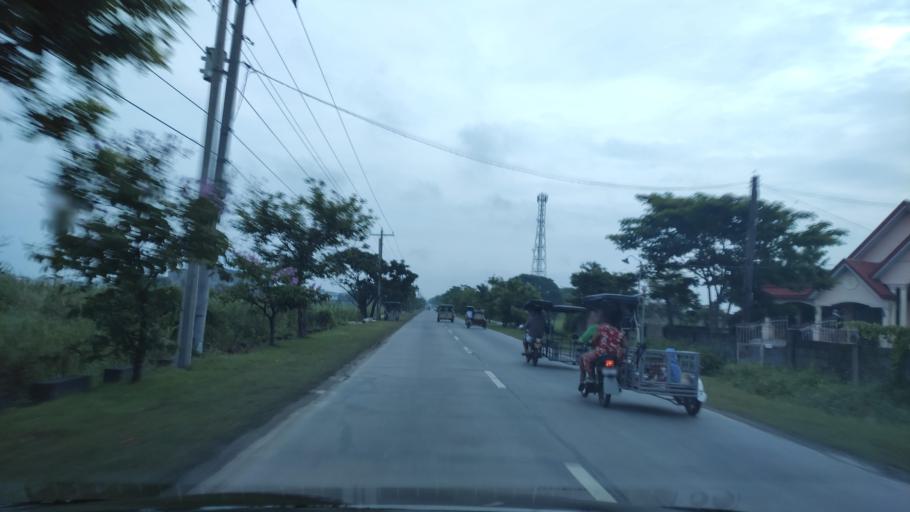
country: PH
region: Central Luzon
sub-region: Province of Pampanga
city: Santo Domingo
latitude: 15.0621
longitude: 120.7547
